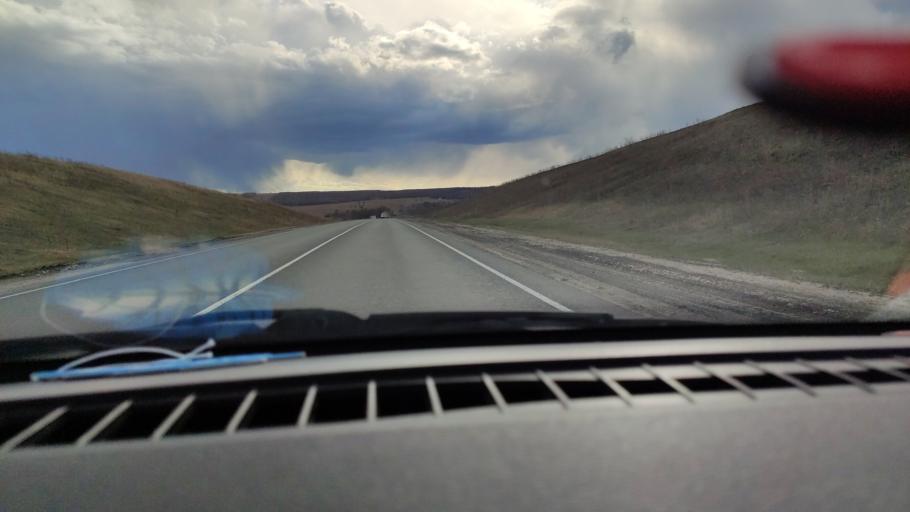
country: RU
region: Saratov
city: Sinodskoye
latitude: 51.9238
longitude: 46.5637
